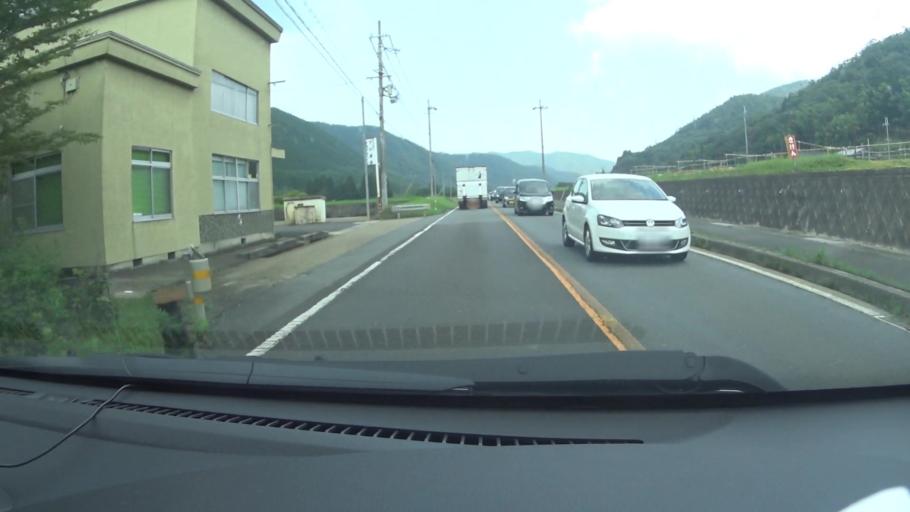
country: JP
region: Kyoto
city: Ayabe
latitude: 35.2241
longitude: 135.4183
